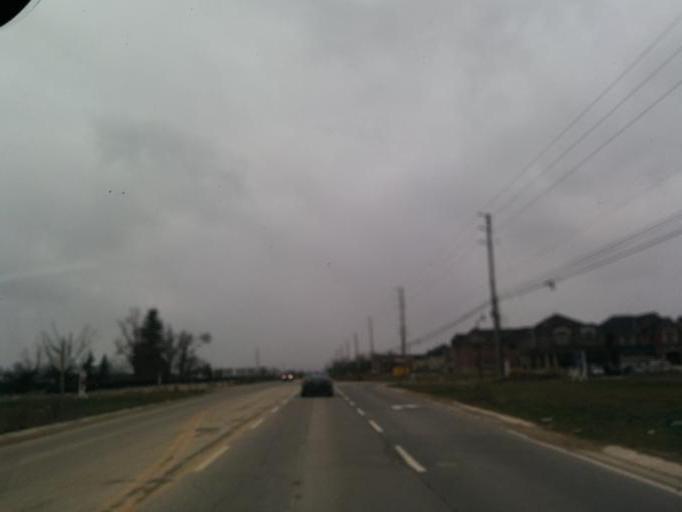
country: CA
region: Ontario
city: Brampton
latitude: 43.7558
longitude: -79.7833
